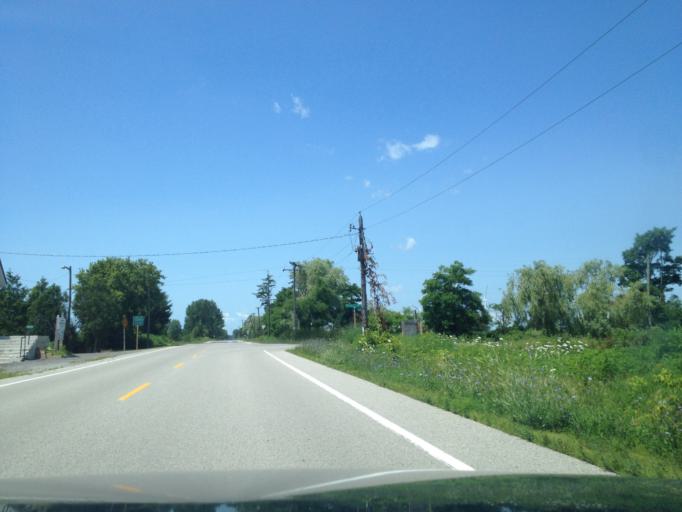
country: CA
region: Ontario
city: Norfolk County
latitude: 42.5787
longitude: -80.5642
